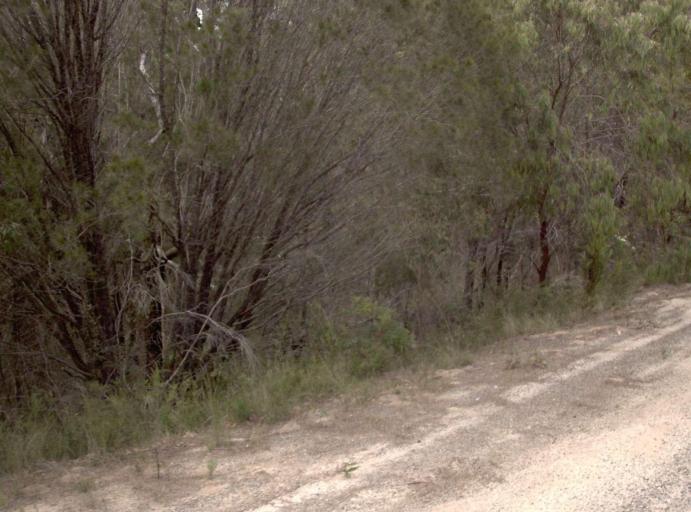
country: AU
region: New South Wales
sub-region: Bega Valley
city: Eden
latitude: -37.4097
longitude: 149.6571
